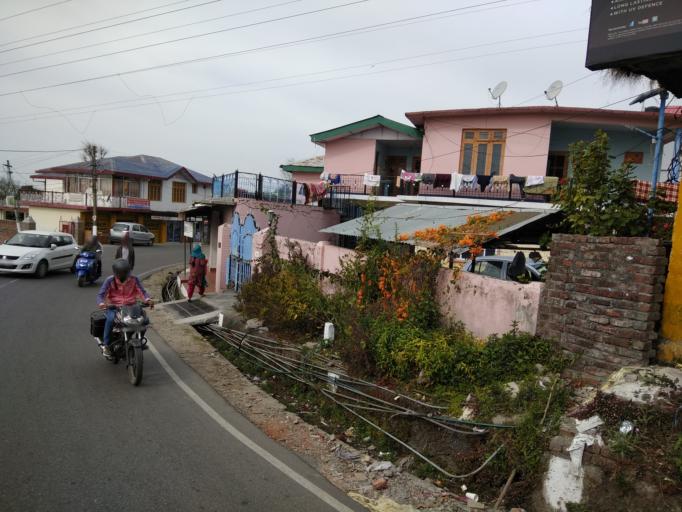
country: IN
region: Himachal Pradesh
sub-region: Kangra
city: Dharmsala
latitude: 32.1899
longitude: 76.3549
